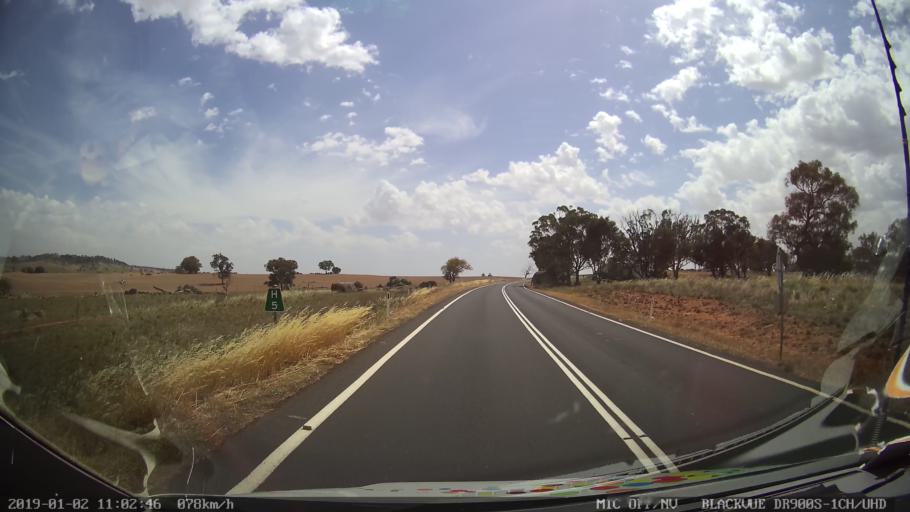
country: AU
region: New South Wales
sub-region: Young
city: Young
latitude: -34.5827
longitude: 148.3298
